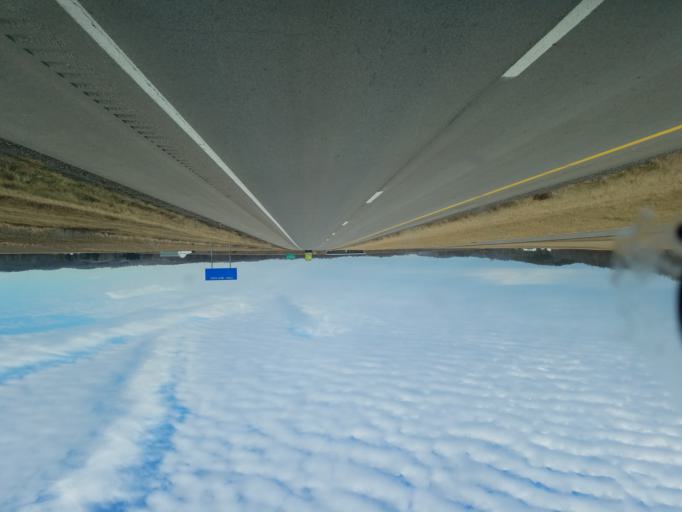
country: US
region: Ohio
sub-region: Muskingum County
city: Frazeysburg
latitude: 40.1276
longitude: -82.1223
